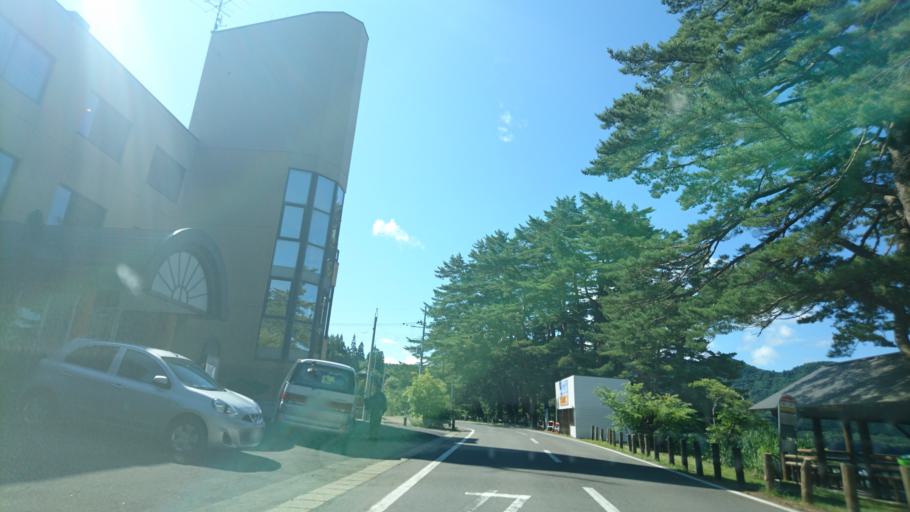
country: JP
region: Akita
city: Kakunodatemachi
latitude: 39.7346
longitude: 140.6972
